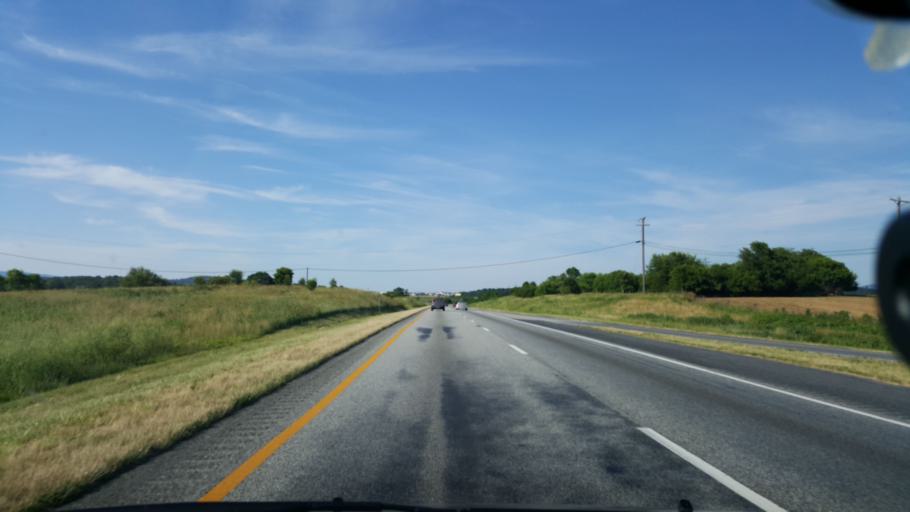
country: US
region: Virginia
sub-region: Rockingham County
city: Bridgewater
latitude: 38.3590
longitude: -78.9257
